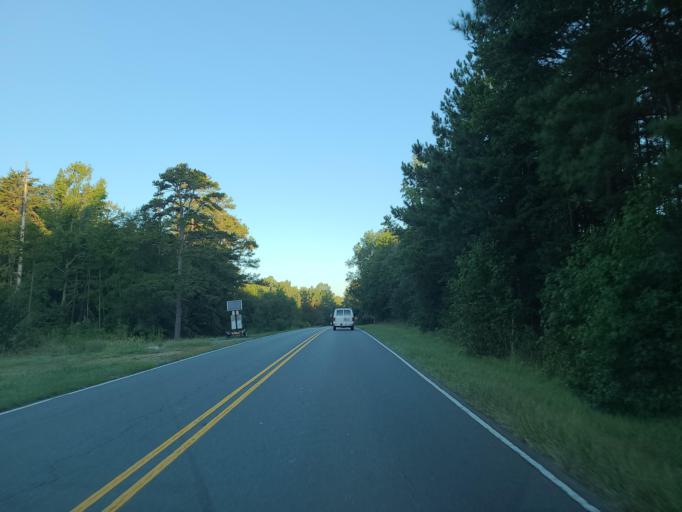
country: US
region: North Carolina
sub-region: Union County
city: Weddington
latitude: 35.0151
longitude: -80.7488
